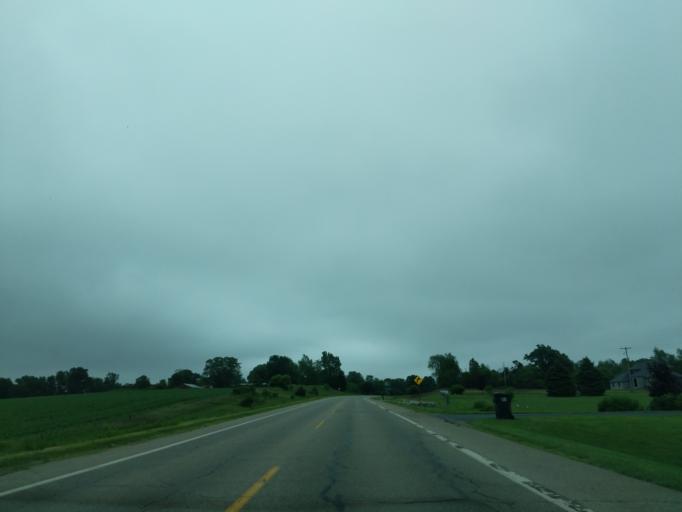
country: US
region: Michigan
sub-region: Hillsdale County
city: Litchfield
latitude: 42.0290
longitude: -84.7142
